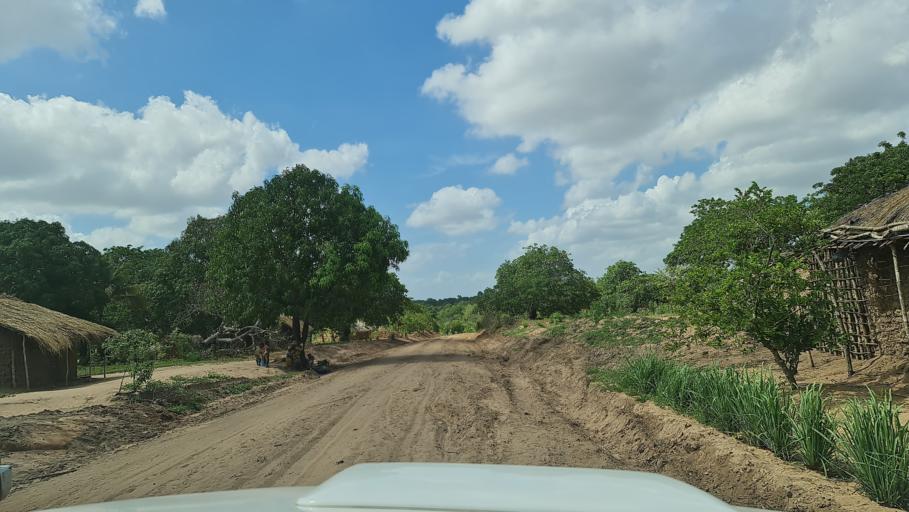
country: MZ
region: Nampula
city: Ilha de Mocambique
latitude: -15.0098
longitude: 40.5607
